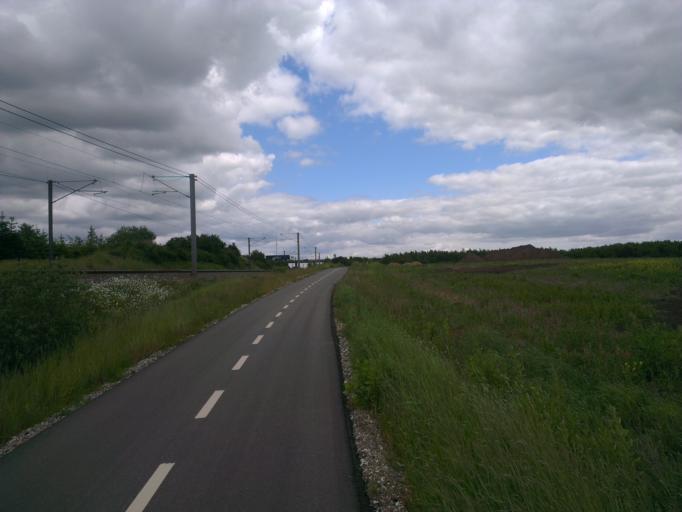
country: DK
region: Capital Region
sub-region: Frederikssund Kommune
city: Frederikssund
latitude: 55.8126
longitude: 12.0980
